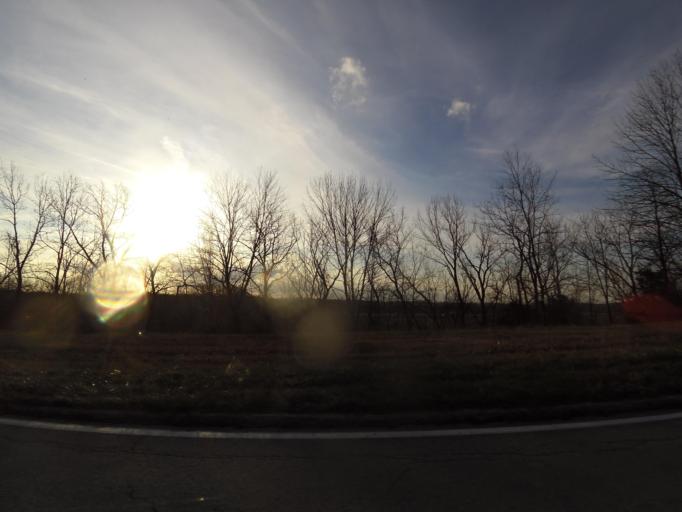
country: US
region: Illinois
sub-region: Fayette County
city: Vandalia
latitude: 38.9232
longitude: -89.2506
